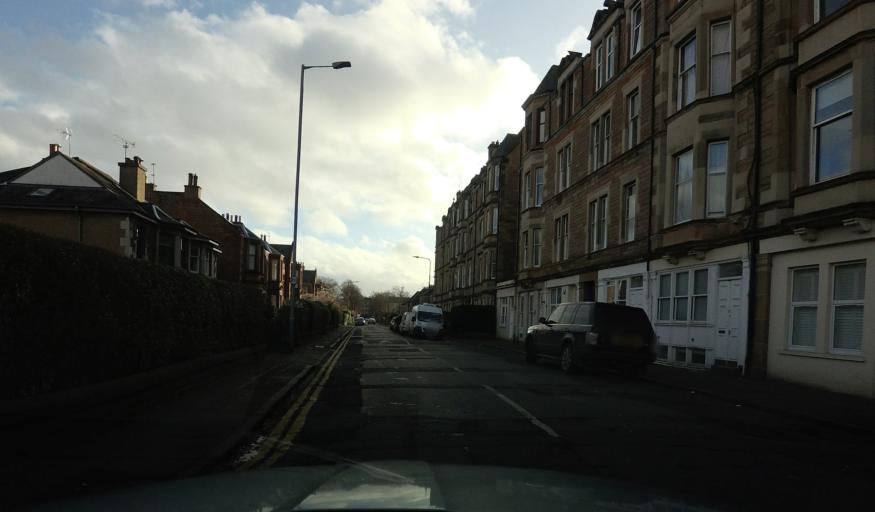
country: GB
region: Scotland
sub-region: Edinburgh
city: Edinburgh
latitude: 55.9744
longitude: -3.2094
